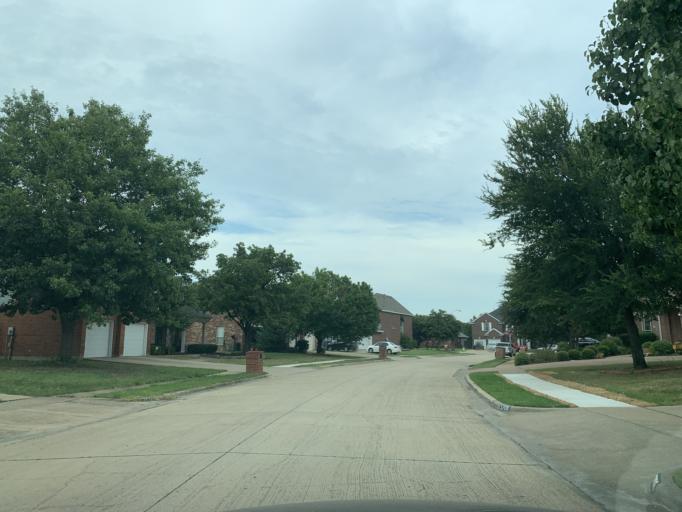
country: US
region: Texas
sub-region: Tarrant County
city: Watauga
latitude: 32.8502
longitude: -97.2884
